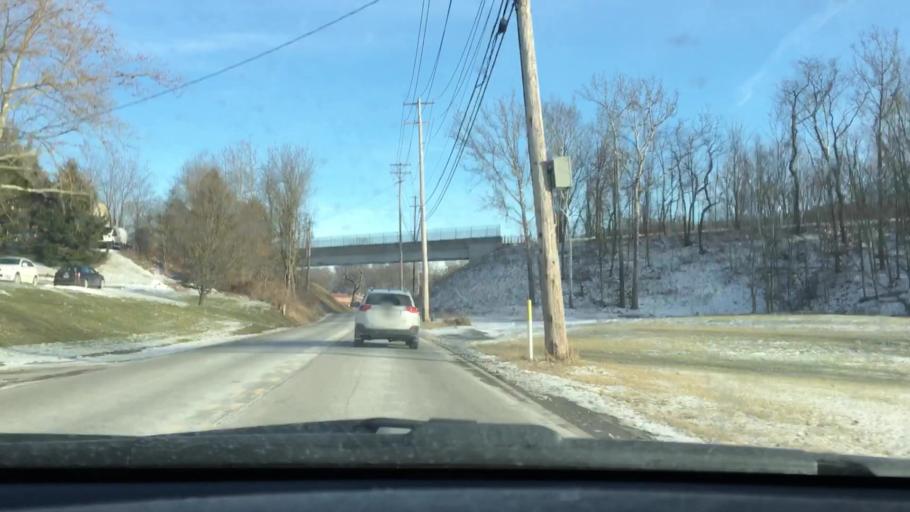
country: US
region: Pennsylvania
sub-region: Washington County
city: McMurray
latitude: 40.2850
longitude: -80.0615
